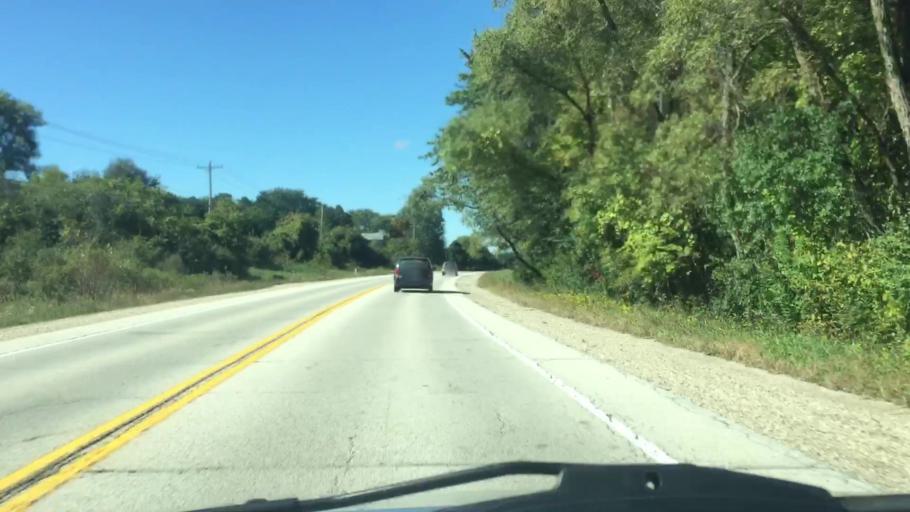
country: US
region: Wisconsin
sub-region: Waukesha County
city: Wales
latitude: 43.0201
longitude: -88.3287
